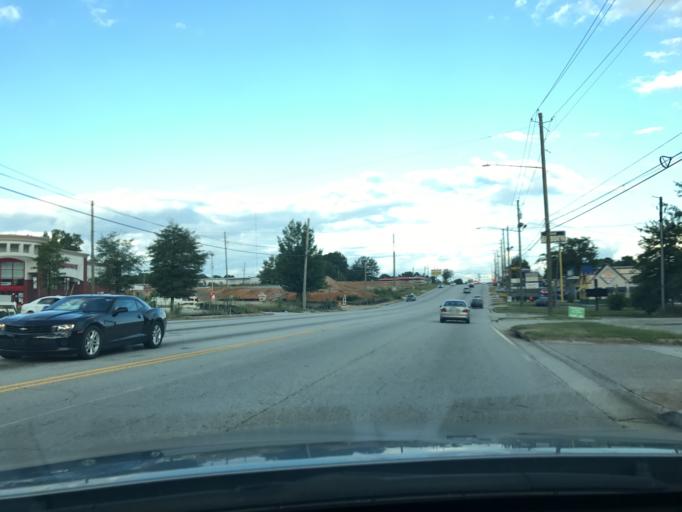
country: US
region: Georgia
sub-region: Douglas County
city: Douglasville
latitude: 33.7511
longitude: -84.7308
